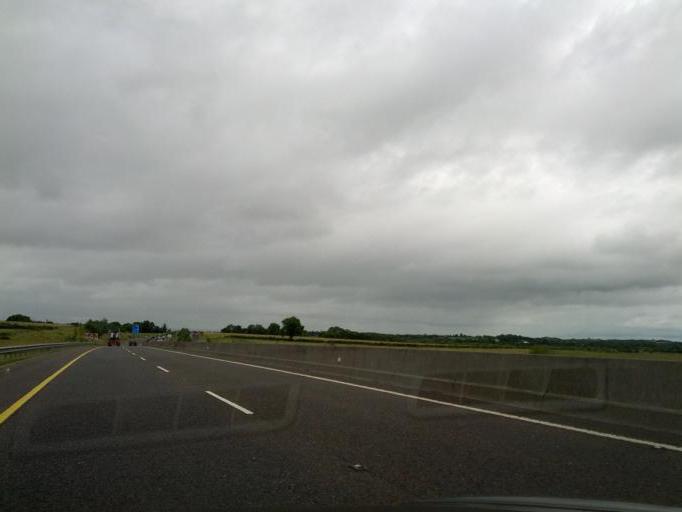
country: IE
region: Munster
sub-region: An Clar
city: Ennis
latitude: 52.8130
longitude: -8.9348
